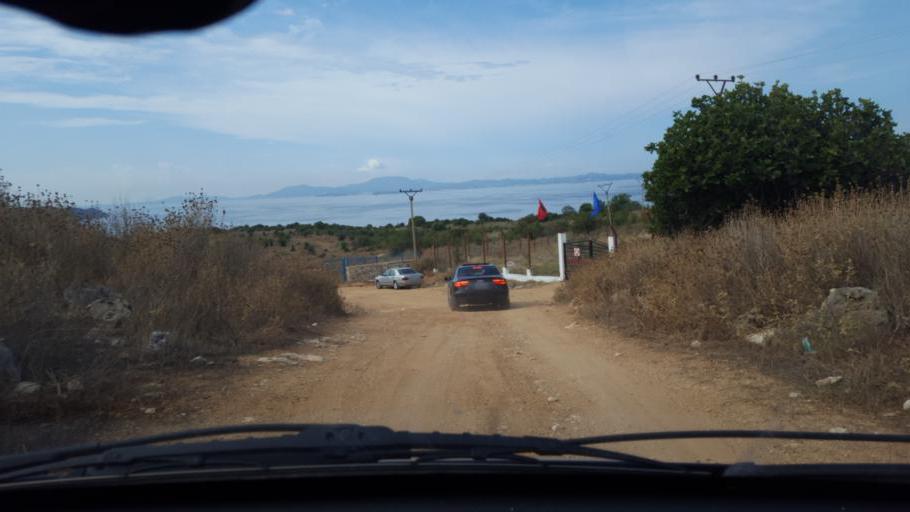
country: AL
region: Vlore
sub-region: Rrethi i Sarandes
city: Xarre
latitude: 39.7538
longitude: 19.9802
